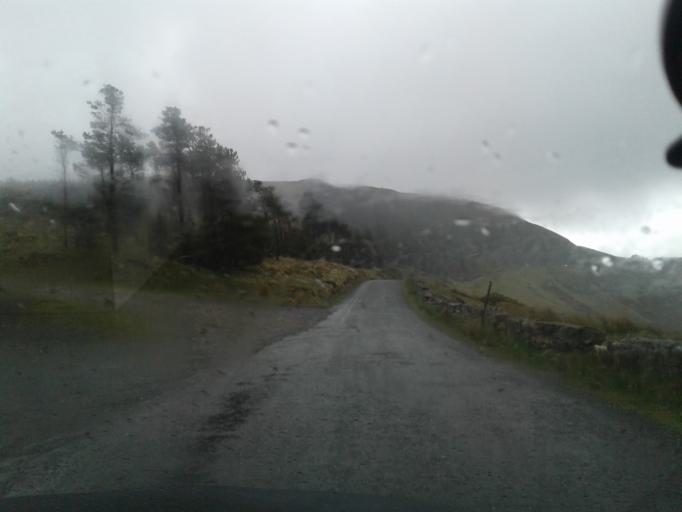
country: IE
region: Leinster
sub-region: Wicklow
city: Enniskerry
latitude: 53.1142
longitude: -6.2636
